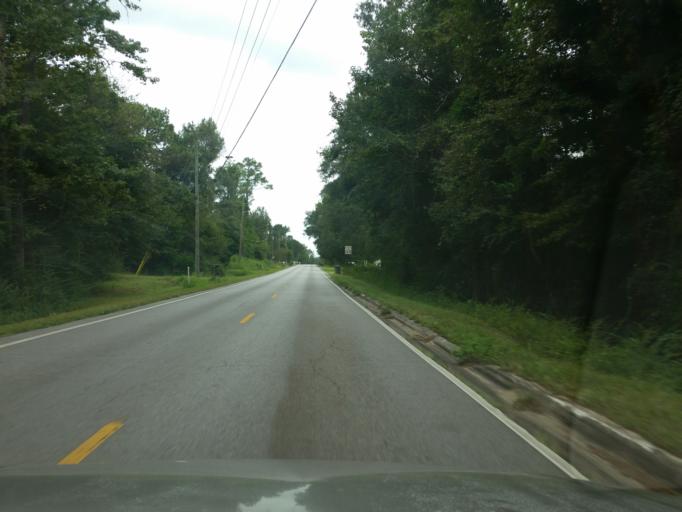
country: US
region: Florida
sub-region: Escambia County
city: Molino
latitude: 30.6861
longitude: -87.3250
